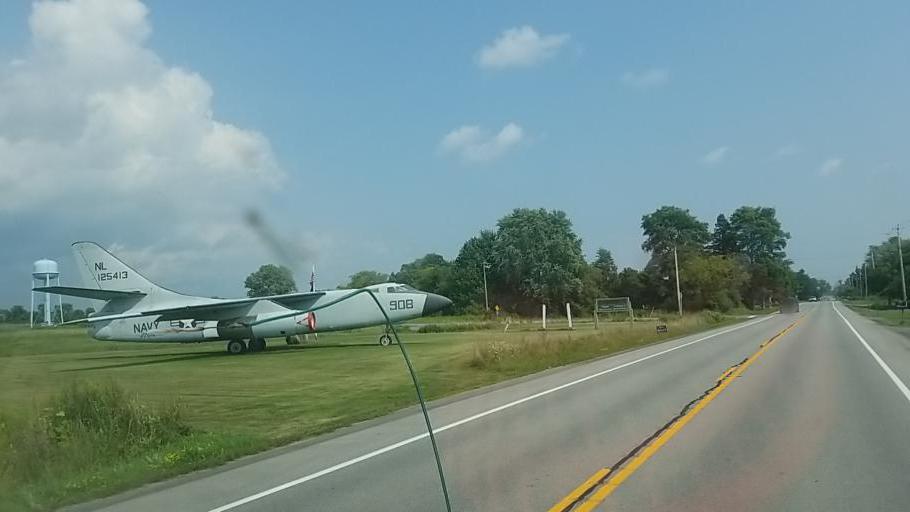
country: US
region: New York
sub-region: Fulton County
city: Johnstown
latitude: 42.9939
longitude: -74.3382
